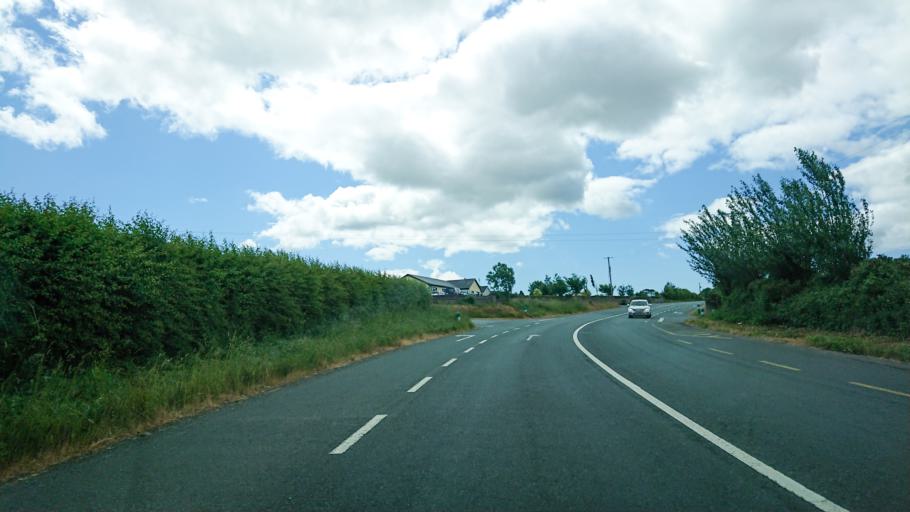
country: IE
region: Munster
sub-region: Waterford
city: Tra Mhor
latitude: 52.2234
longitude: -7.1991
